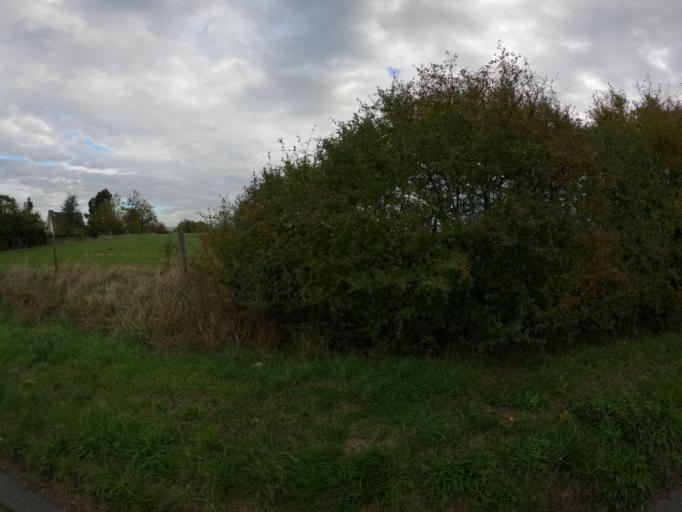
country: FR
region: Ile-de-France
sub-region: Departement de Seine-et-Marne
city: Montry
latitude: 48.8744
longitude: 2.8280
